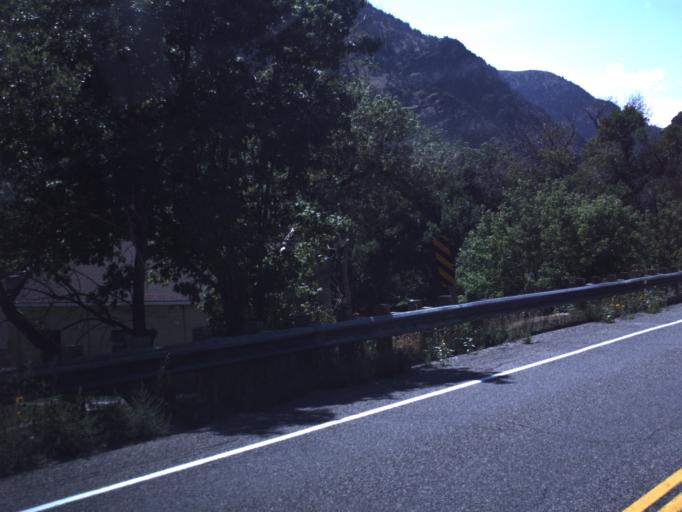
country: US
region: Utah
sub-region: Cache County
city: North Logan
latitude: 41.7468
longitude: -111.7455
